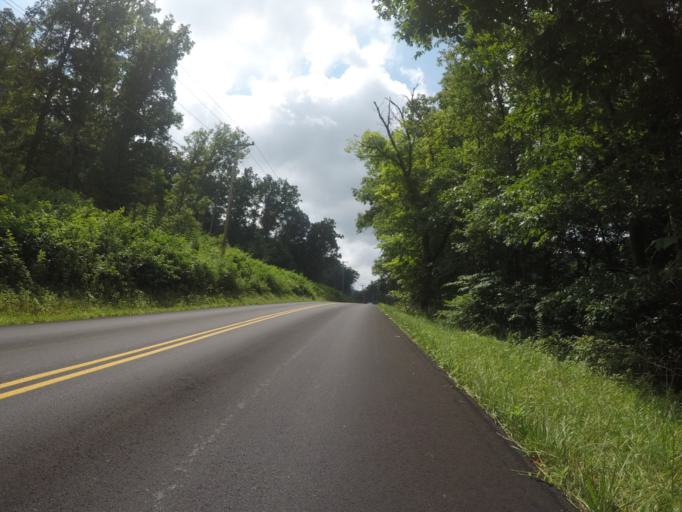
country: US
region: Kentucky
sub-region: Boyd County
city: Meads
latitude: 38.4030
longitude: -82.6583
